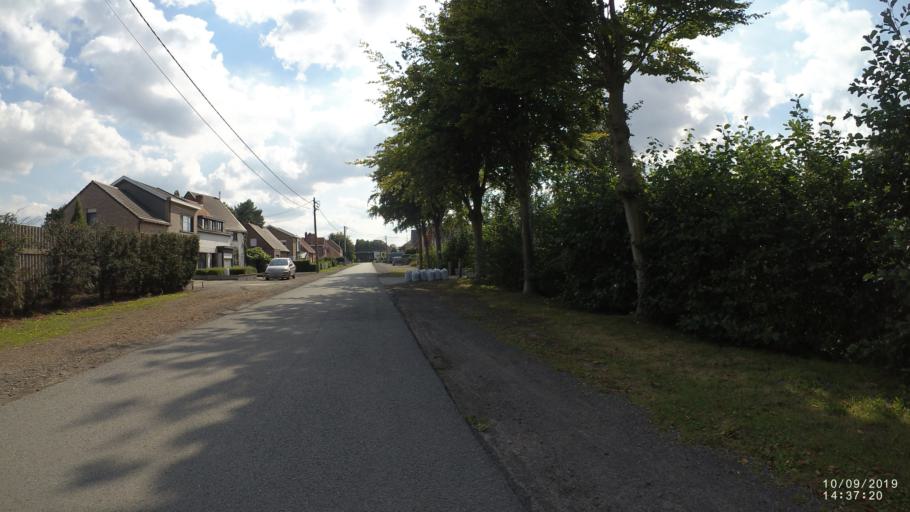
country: BE
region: Flanders
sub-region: Provincie Oost-Vlaanderen
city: Kaprijke
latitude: 51.1896
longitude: 3.6816
